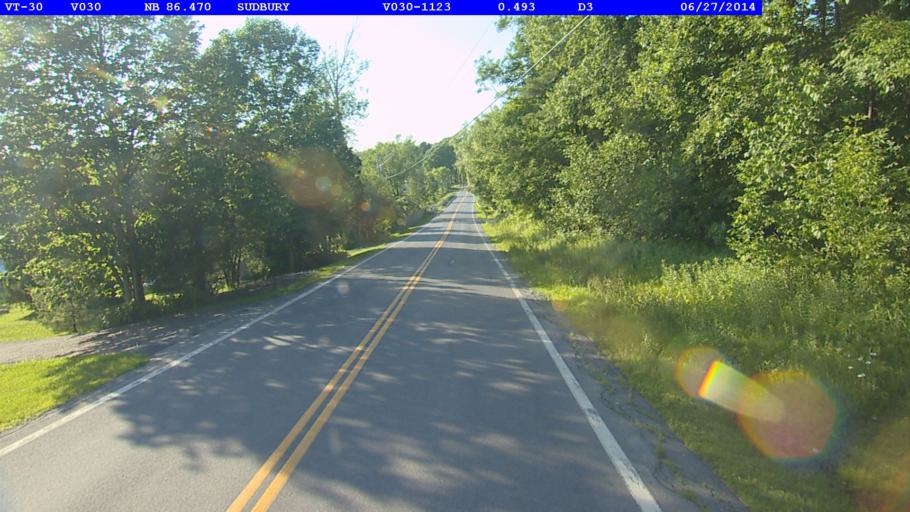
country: US
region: Vermont
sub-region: Rutland County
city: Brandon
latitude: 43.7567
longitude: -73.1931
